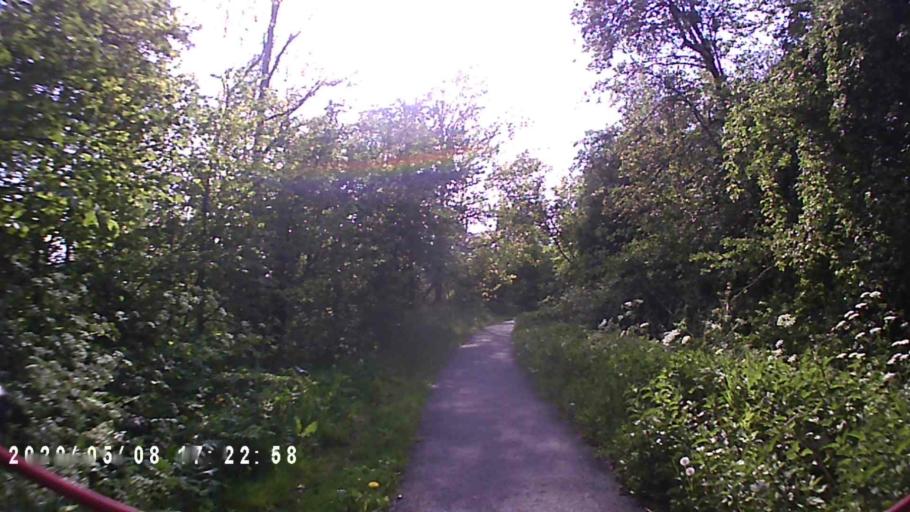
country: NL
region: Groningen
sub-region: Gemeente Winsum
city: Winsum
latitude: 53.3817
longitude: 6.5509
